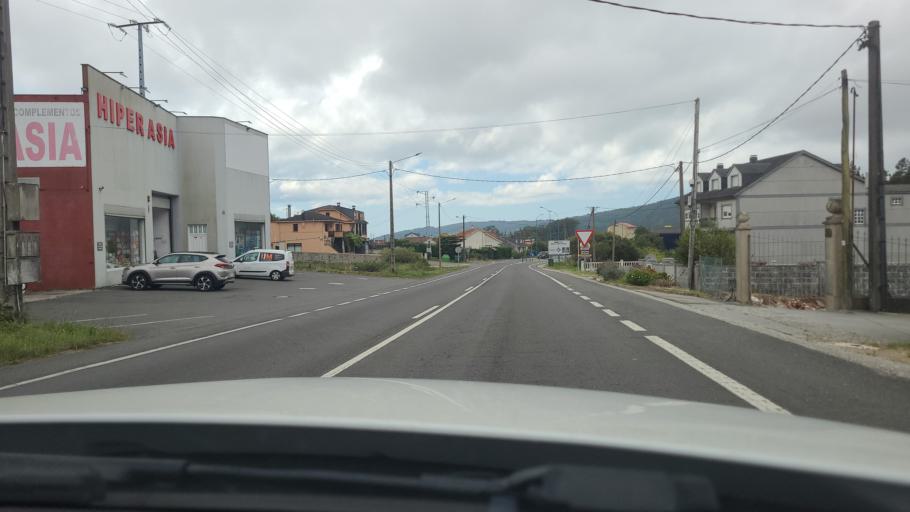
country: ES
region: Galicia
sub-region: Provincia da Coruna
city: Cee
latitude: 42.9738
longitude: -9.1899
